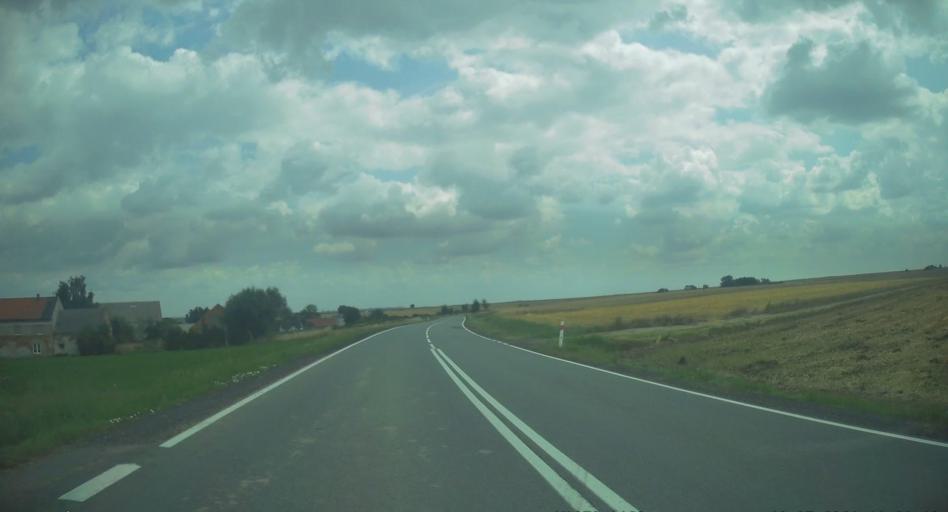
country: PL
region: Opole Voivodeship
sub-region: Powiat prudnicki
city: Raclawice Slaskie
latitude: 50.3496
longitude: 17.7746
